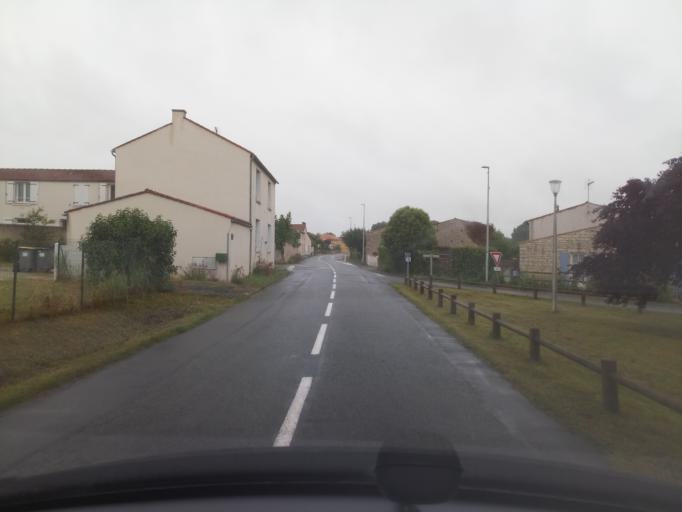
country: FR
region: Poitou-Charentes
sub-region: Departement de la Charente-Maritime
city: Verines
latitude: 46.2279
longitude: -0.9890
